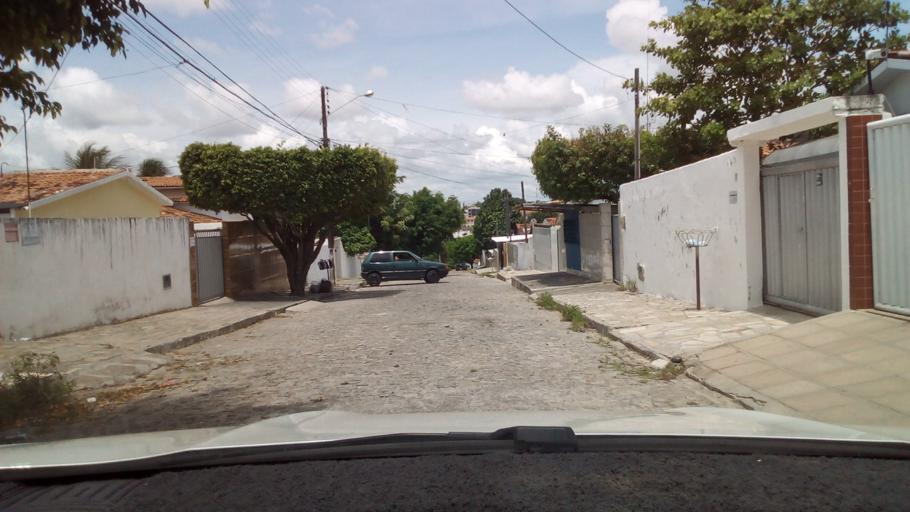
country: BR
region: Paraiba
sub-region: Joao Pessoa
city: Joao Pessoa
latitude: -7.1828
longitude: -34.8478
